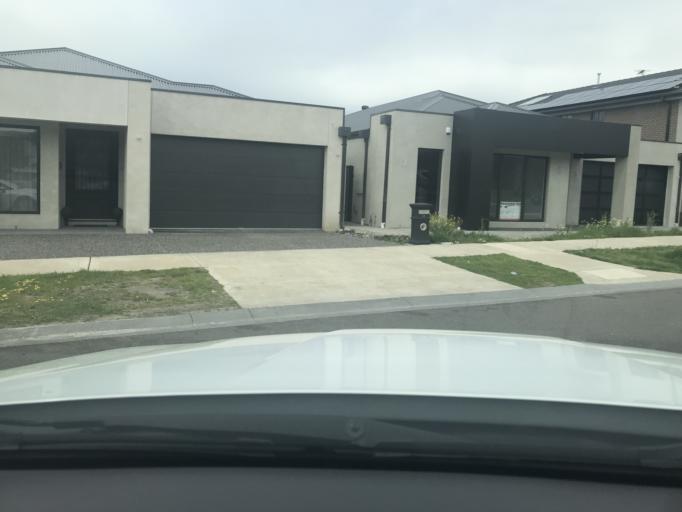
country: AU
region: Victoria
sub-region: Hume
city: Roxburgh Park
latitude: -37.6004
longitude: 144.9085
